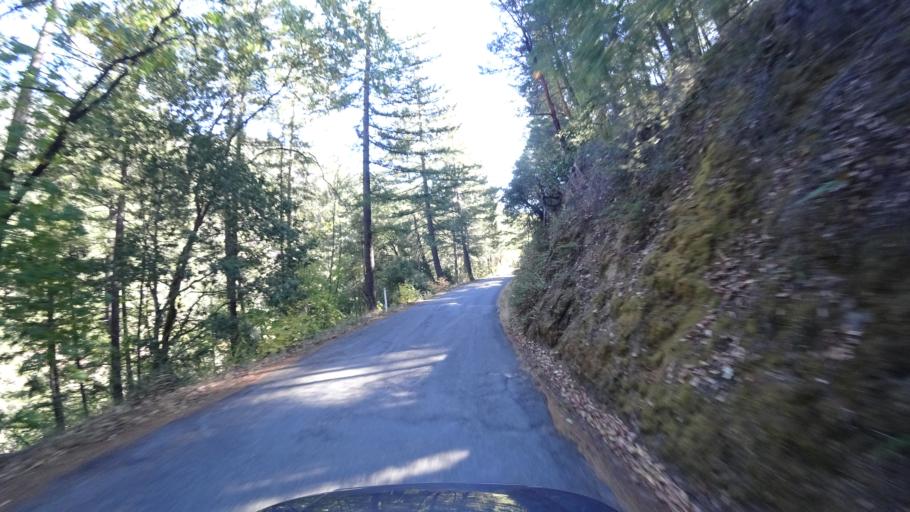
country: US
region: California
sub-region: Humboldt County
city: Willow Creek
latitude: 41.3163
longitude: -123.3789
